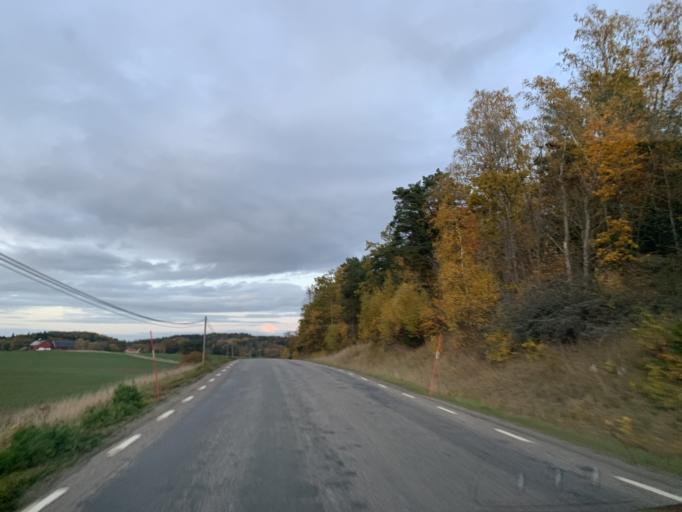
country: SE
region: Stockholm
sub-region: Nynashamns Kommun
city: Osmo
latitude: 58.9493
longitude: 17.7646
